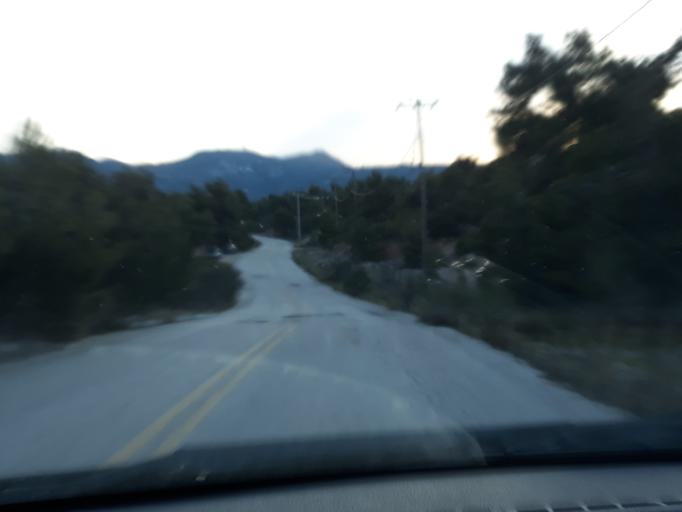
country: GR
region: Attica
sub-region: Nomarchia Anatolikis Attikis
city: Afidnes
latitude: 38.2073
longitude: 23.7975
